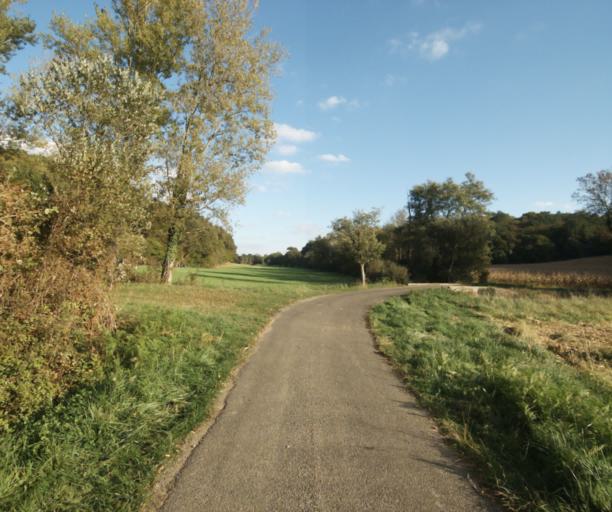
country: FR
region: Midi-Pyrenees
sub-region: Departement du Gers
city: Eauze
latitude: 43.7621
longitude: 0.0938
